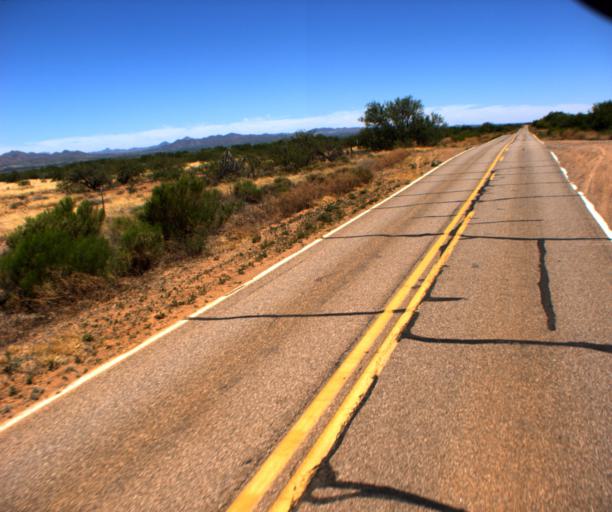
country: US
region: Arizona
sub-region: Pima County
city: Three Points
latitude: 31.7251
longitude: -111.4880
